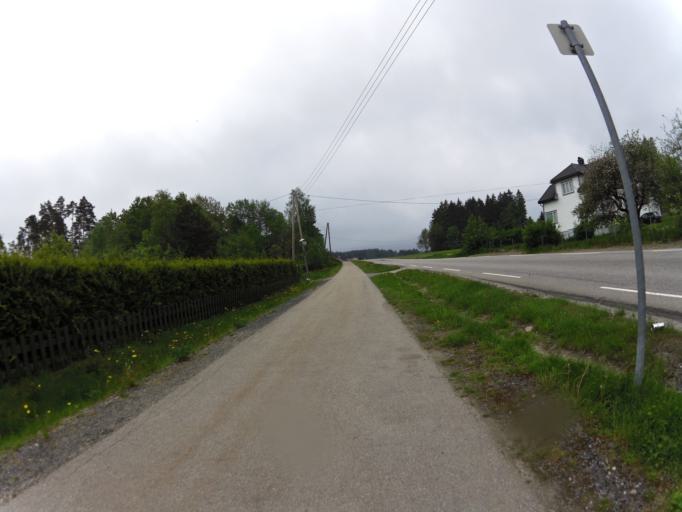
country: NO
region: Ostfold
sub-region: Rygge
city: Ryggebyen
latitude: 59.3647
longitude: 10.7243
